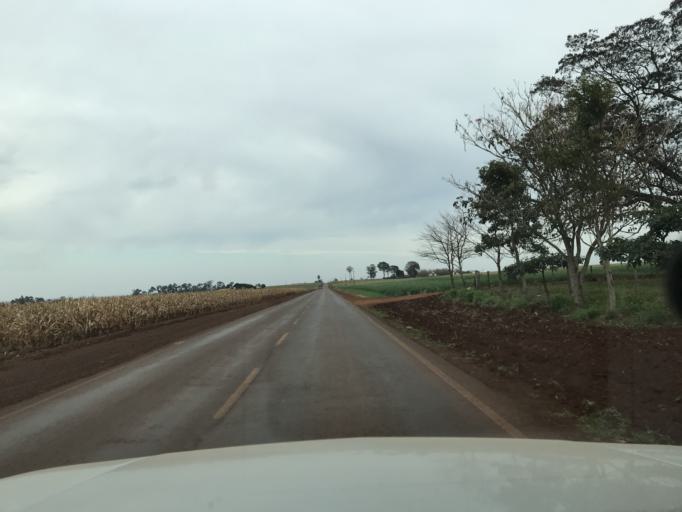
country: BR
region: Parana
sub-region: Palotina
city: Palotina
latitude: -24.4205
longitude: -53.8859
